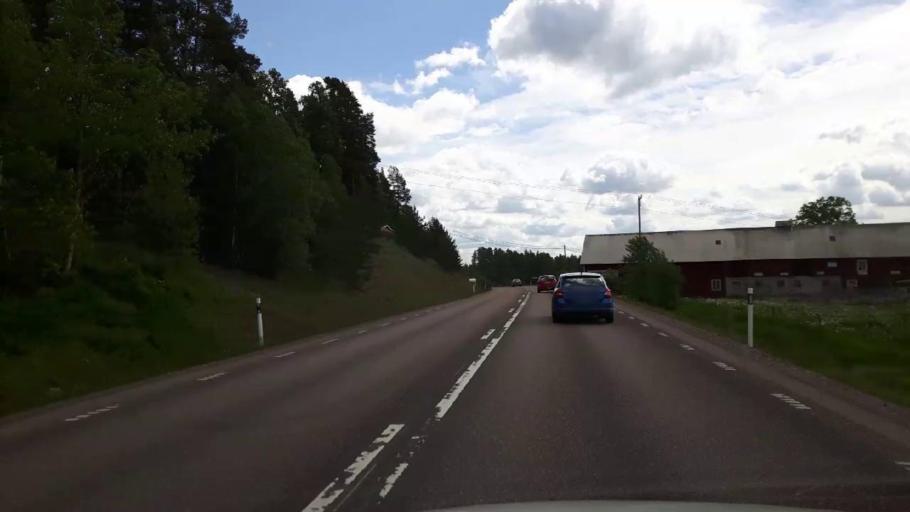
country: SE
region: Dalarna
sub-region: Saters Kommun
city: Saeter
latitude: 60.4367
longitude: 15.8229
